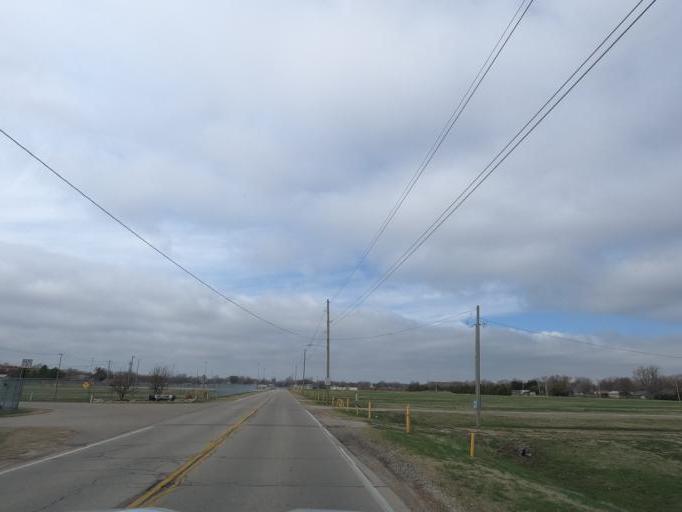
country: US
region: Kansas
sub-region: Reno County
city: Hutchinson
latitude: 38.0811
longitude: -97.9238
